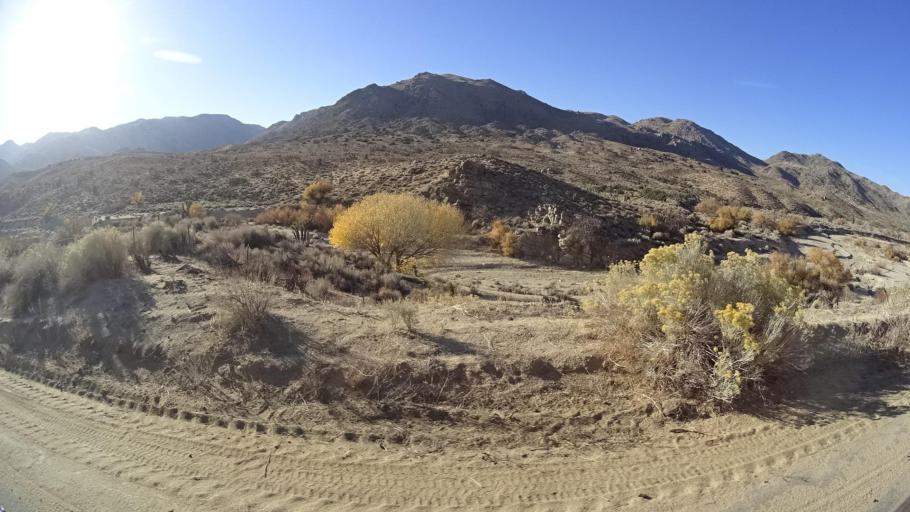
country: US
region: California
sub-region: Kern County
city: Weldon
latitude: 35.4893
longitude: -118.2042
